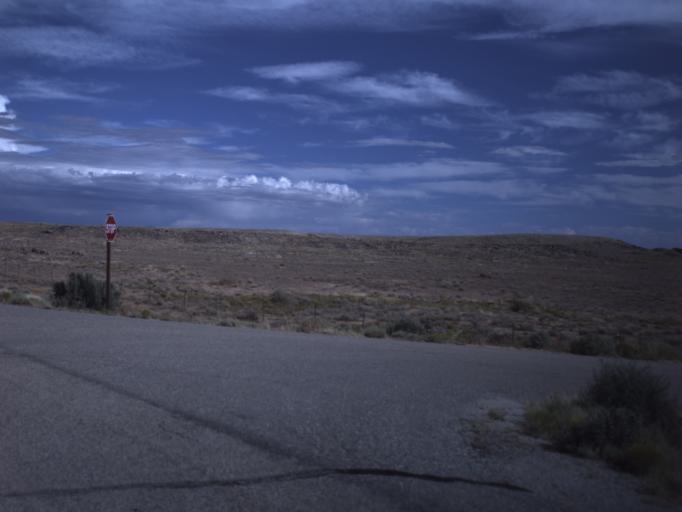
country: US
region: Colorado
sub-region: Montezuma County
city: Towaoc
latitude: 37.1779
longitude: -109.1213
